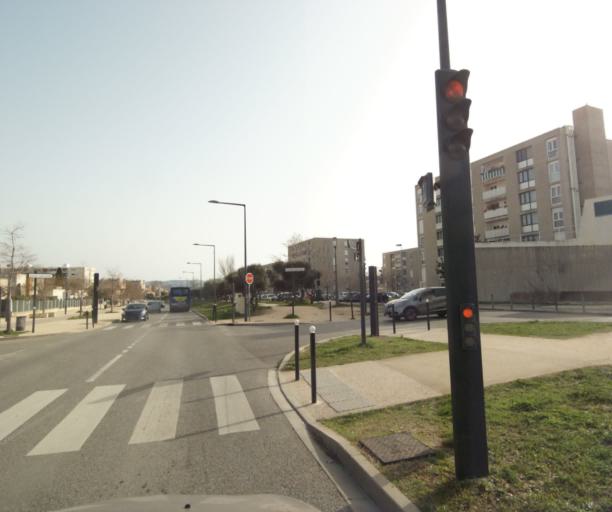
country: FR
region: Provence-Alpes-Cote d'Azur
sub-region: Departement des Bouches-du-Rhone
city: Vitrolles
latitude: 43.4417
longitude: 5.2531
